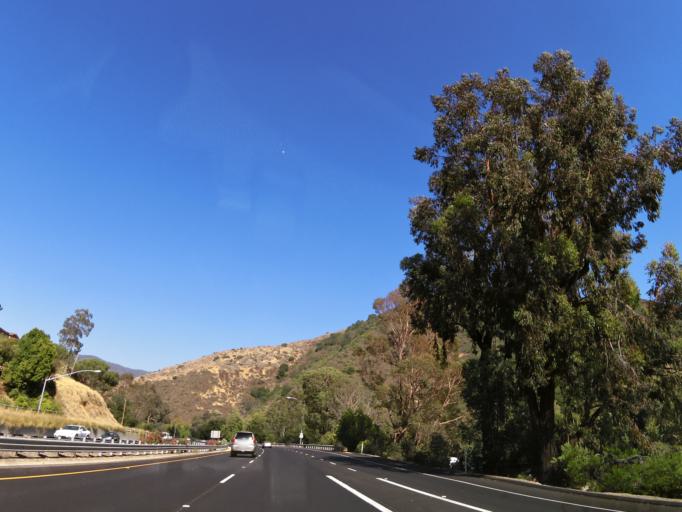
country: US
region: California
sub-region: San Luis Obispo County
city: San Luis Obispo
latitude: 35.2917
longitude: -120.6480
